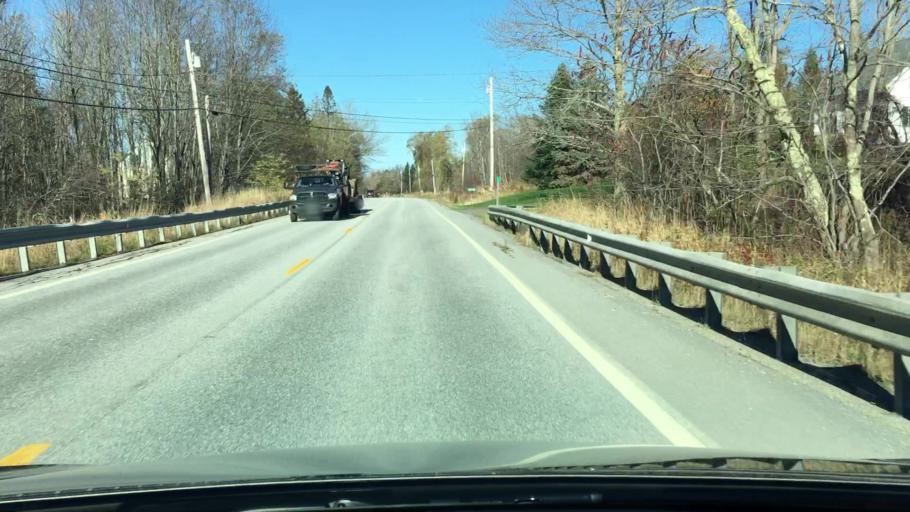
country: US
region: Maine
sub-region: Waldo County
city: Winterport
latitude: 44.6435
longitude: -68.8261
